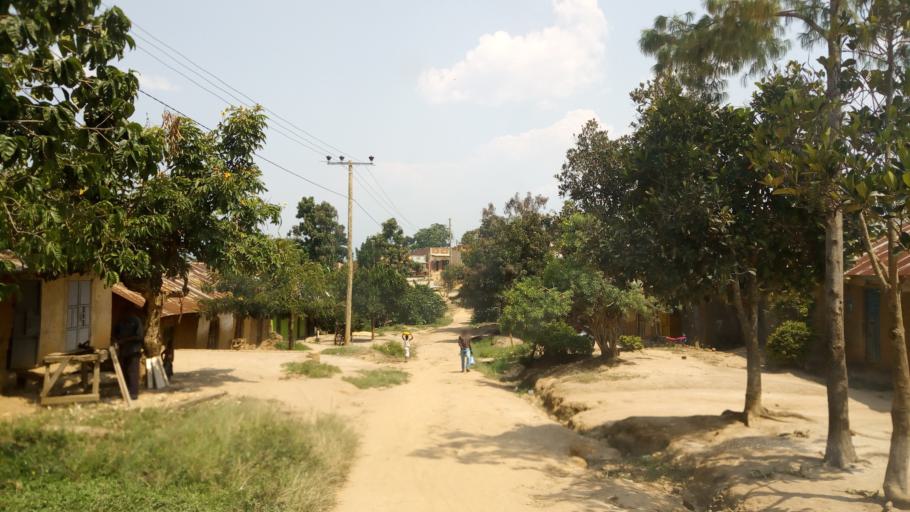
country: UG
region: Western Region
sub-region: Kanungu District
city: Ntungamo
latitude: -0.8054
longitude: 29.6451
